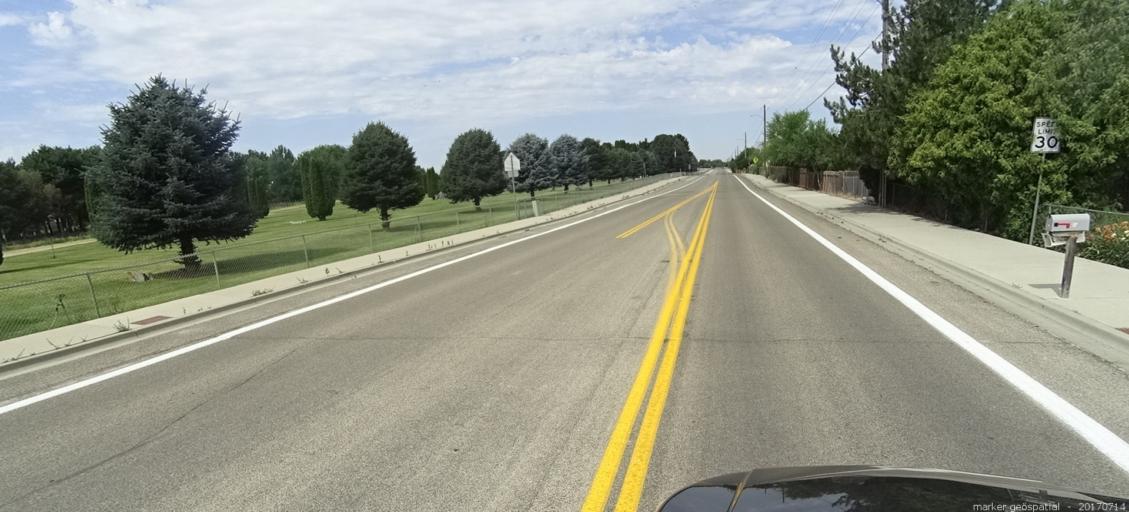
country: US
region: Idaho
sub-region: Ada County
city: Kuna
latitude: 43.4957
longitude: -116.4242
